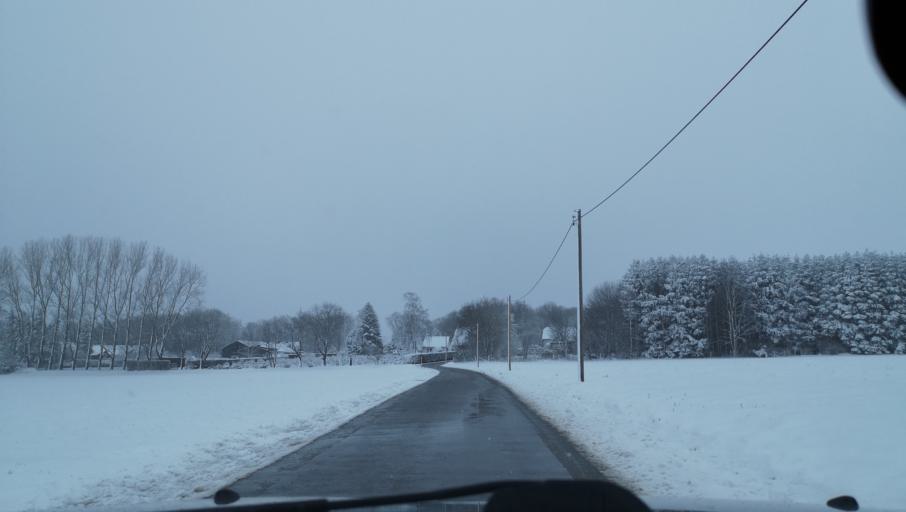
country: DE
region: North Rhine-Westphalia
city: Radevormwald
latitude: 51.2342
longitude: 7.3622
